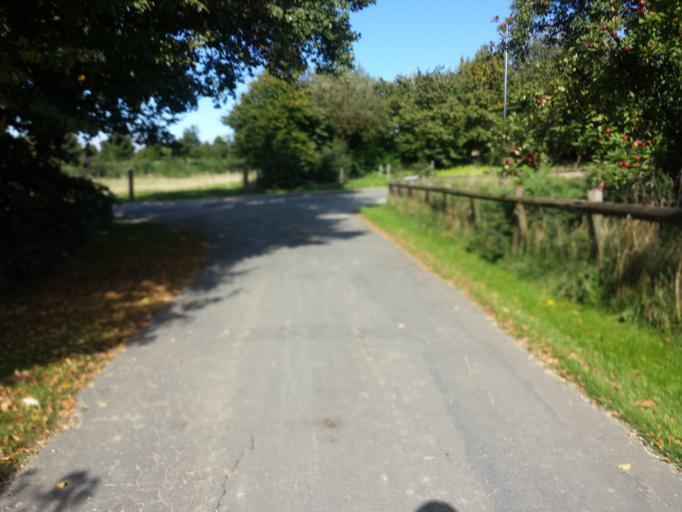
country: DE
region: North Rhine-Westphalia
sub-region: Regierungsbezirk Detmold
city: Langenberg
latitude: 51.7696
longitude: 8.3103
